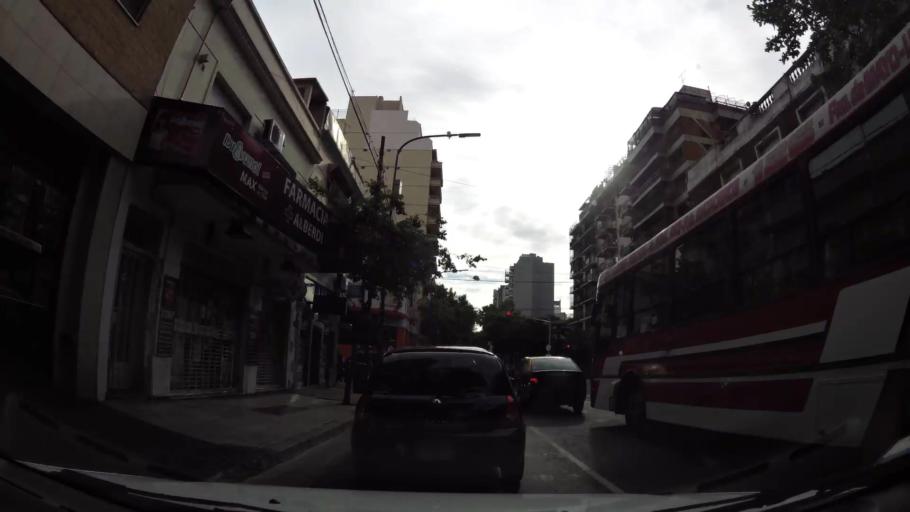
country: AR
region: Buenos Aires F.D.
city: Villa Santa Rita
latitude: -34.6303
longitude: -58.4583
